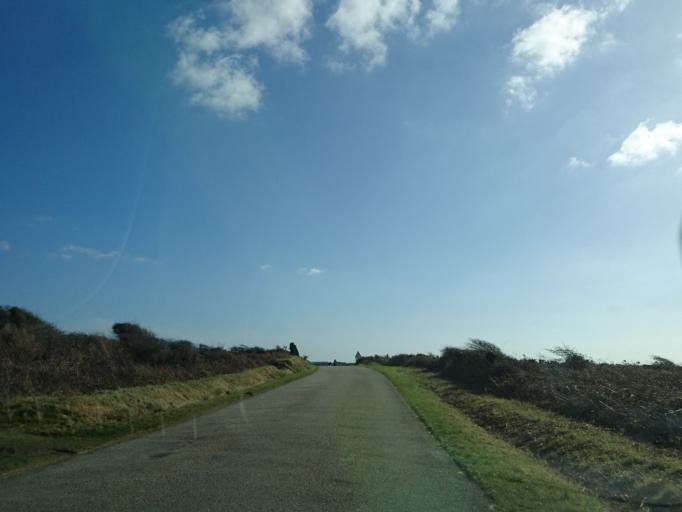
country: FR
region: Brittany
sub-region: Departement du Finistere
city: Roscanvel
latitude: 48.3137
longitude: -4.5713
